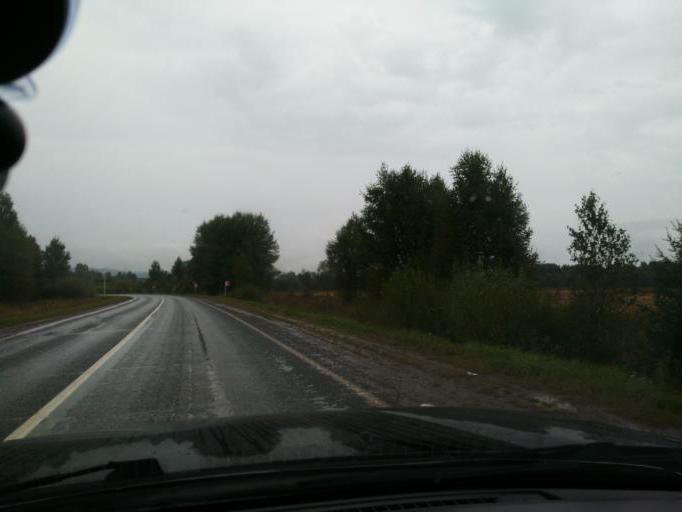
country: RU
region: Perm
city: Yugo-Kamskiy
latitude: 57.5326
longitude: 55.6895
